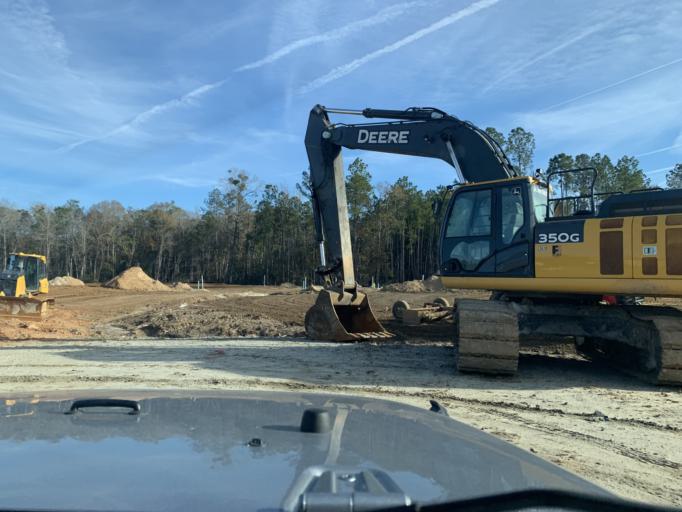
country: US
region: Georgia
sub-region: Chatham County
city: Pooler
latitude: 32.0678
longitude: -81.2543
